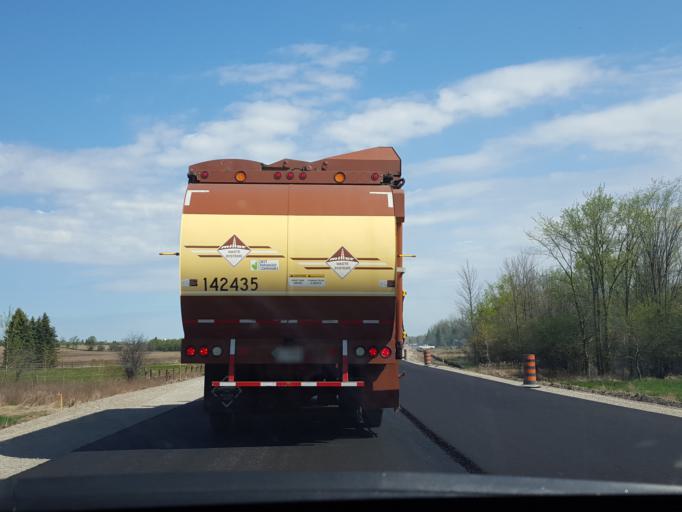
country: CA
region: Ontario
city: Uxbridge
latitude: 44.0723
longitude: -78.9355
